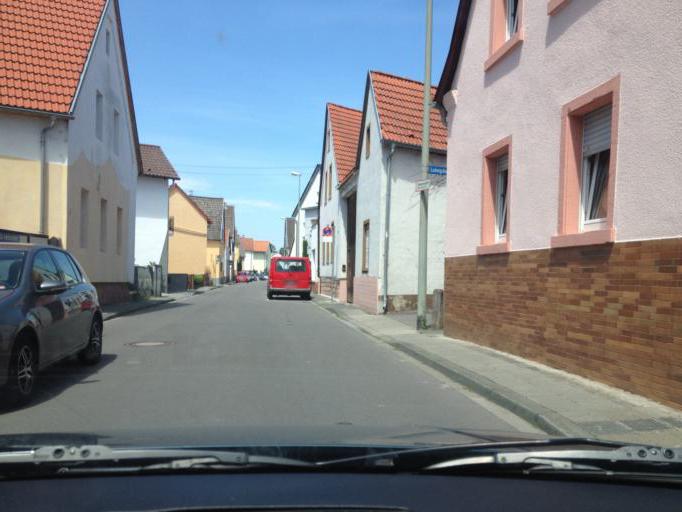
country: DE
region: Rheinland-Pfalz
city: Neuhofen
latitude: 49.4243
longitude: 8.4260
